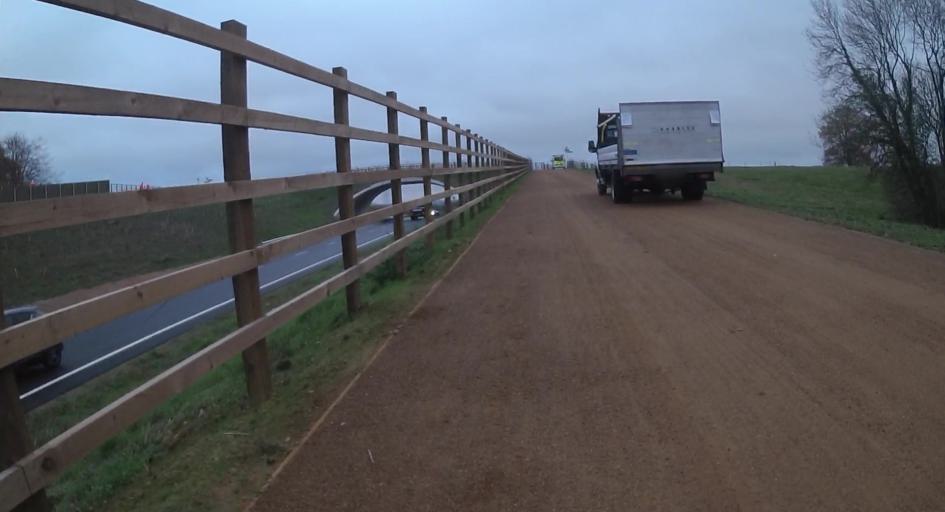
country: GB
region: England
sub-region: West Berkshire
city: Arborfield
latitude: 51.3908
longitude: -0.9128
